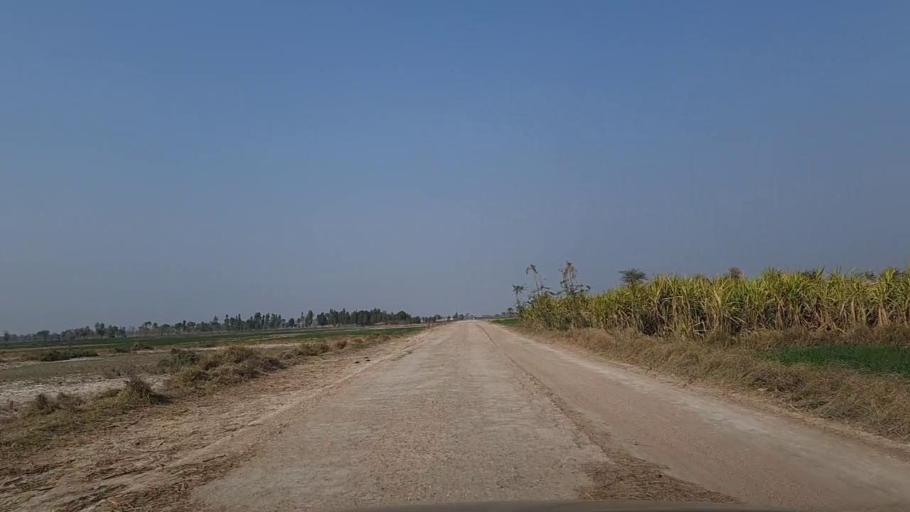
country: PK
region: Sindh
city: Daur
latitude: 26.4105
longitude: 68.4087
